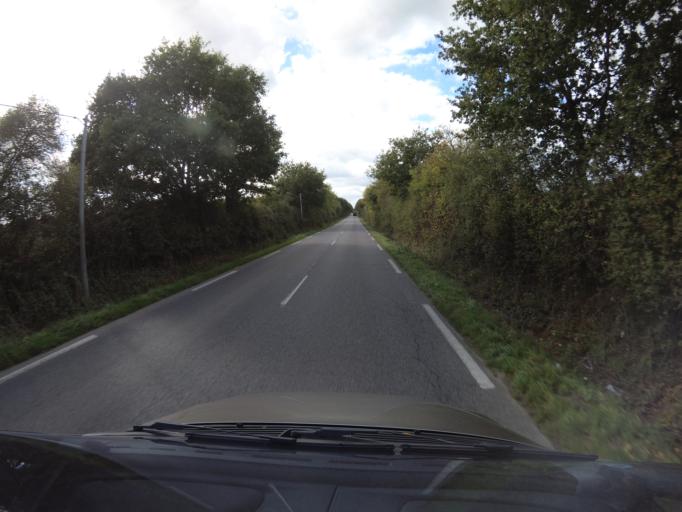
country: FR
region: Pays de la Loire
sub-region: Departement de la Loire-Atlantique
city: Heric
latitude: 47.4121
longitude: -1.6893
